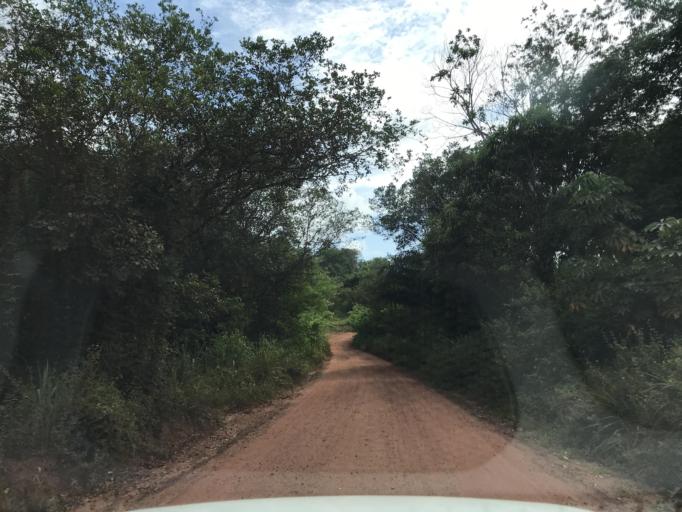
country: BR
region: Bahia
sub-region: Entre Rios
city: Entre Rios
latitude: -12.1786
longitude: -38.1245
